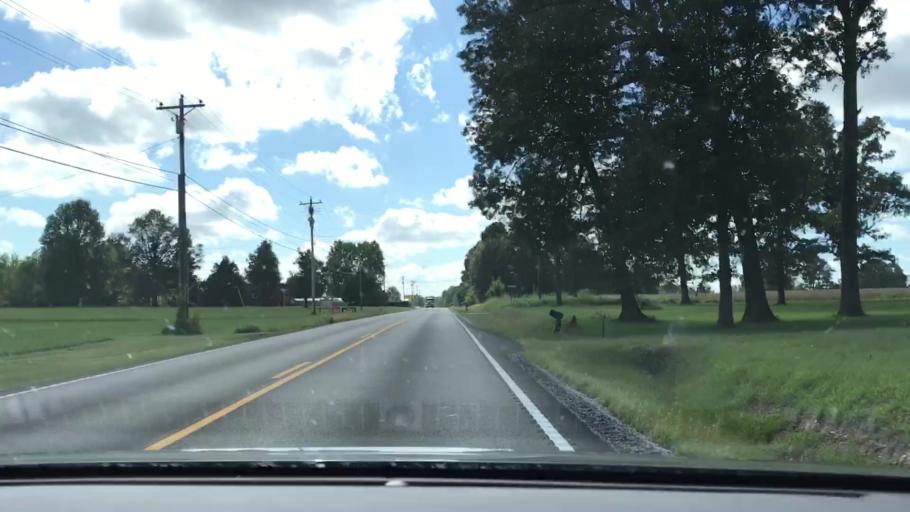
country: US
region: Kentucky
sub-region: Graves County
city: Mayfield
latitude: 36.7667
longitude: -88.5961
